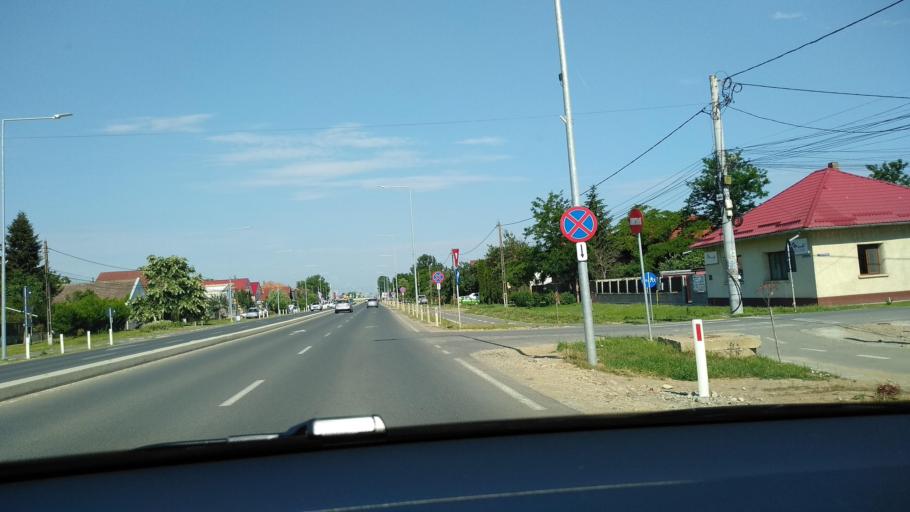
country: RO
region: Timis
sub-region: Comuna Mosnita Noua
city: Mosnita Noua
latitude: 45.7191
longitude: 21.3226
